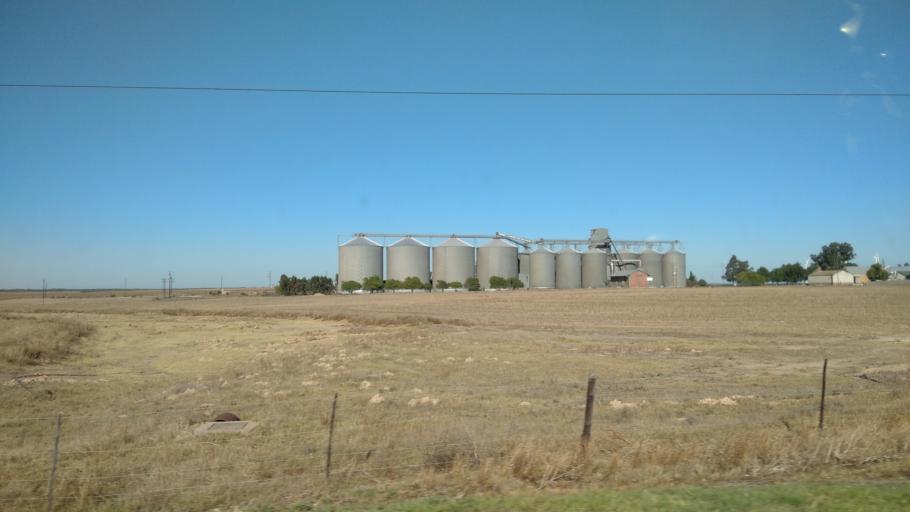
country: ZA
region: Western Cape
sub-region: West Coast District Municipality
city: Moorreesburg
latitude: -33.0998
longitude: 18.4212
